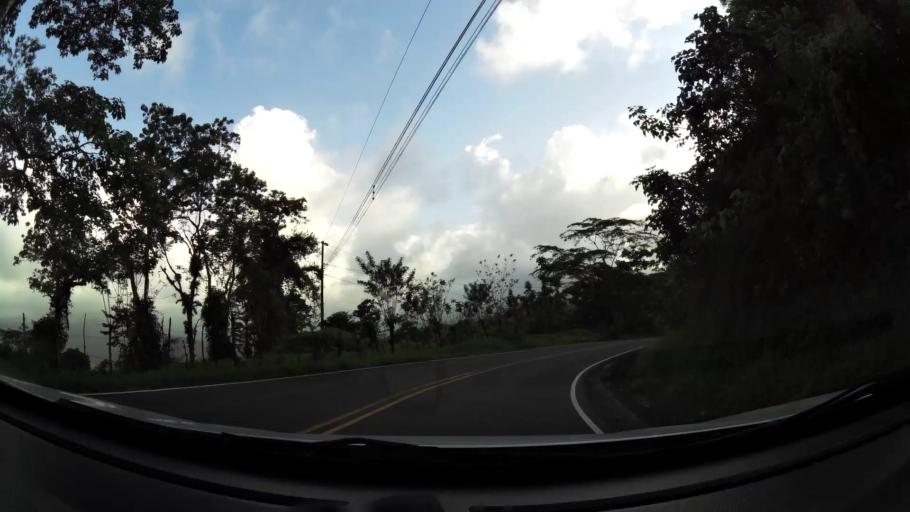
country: CR
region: Limon
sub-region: Canton de Siquirres
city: Siquirres
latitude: 10.0202
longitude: -83.5627
